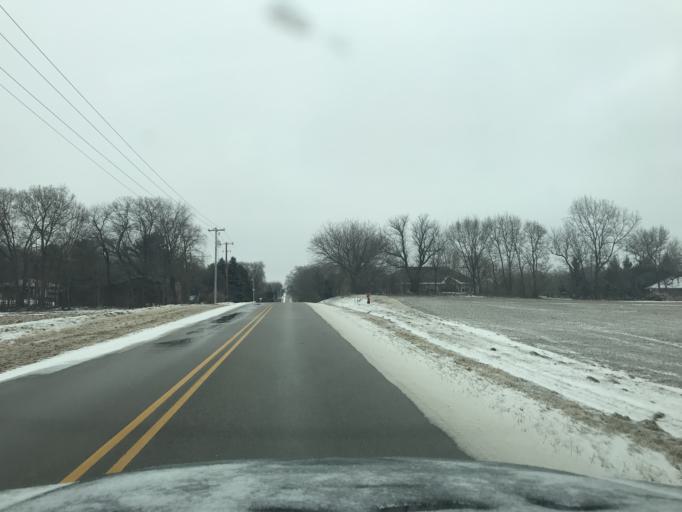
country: US
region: Wisconsin
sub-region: Dane County
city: Cottage Grove
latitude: 43.1045
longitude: -89.2208
